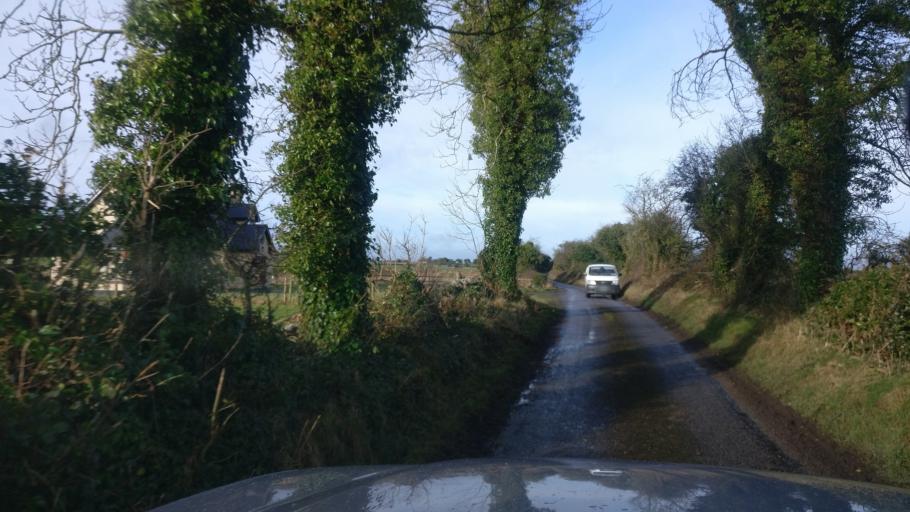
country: IE
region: Connaught
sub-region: County Galway
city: Loughrea
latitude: 53.2004
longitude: -8.6654
